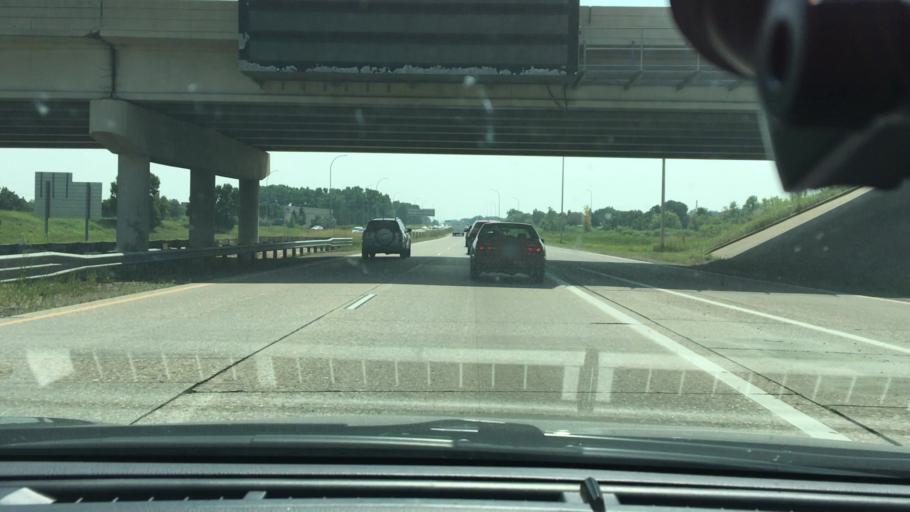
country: US
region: Minnesota
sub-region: Hennepin County
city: Osseo
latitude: 45.0948
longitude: -93.4026
